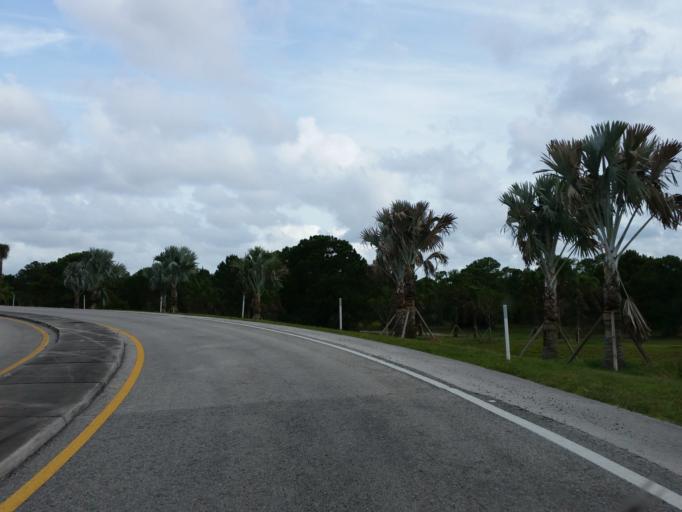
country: US
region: Florida
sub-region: Saint Lucie County
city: Port Saint Lucie
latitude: 27.2765
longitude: -80.3621
